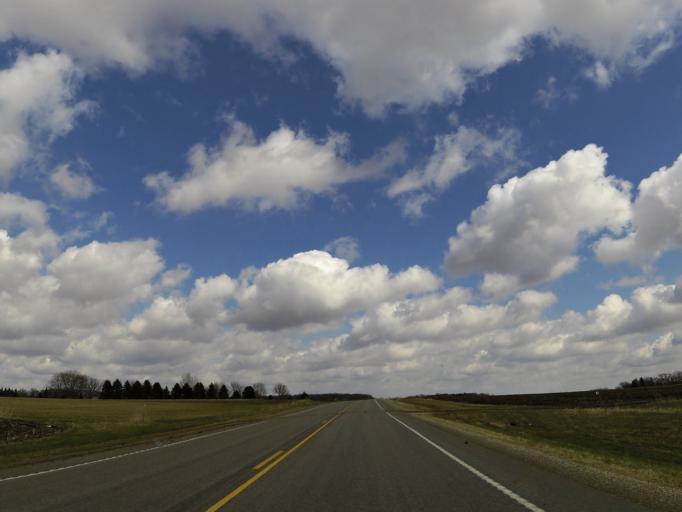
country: US
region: Minnesota
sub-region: Dodge County
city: Mantorville
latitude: 44.0797
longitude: -92.6990
